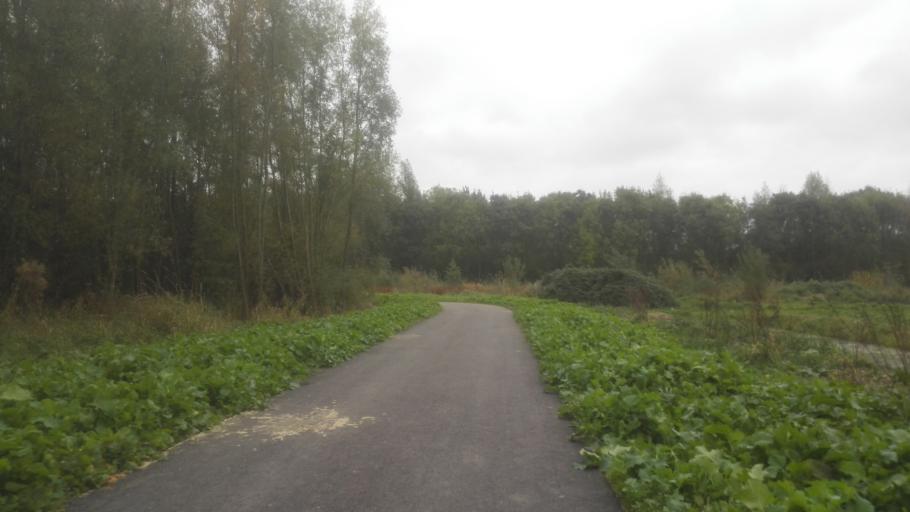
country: NL
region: South Holland
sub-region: Gemeente Delft
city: Delft
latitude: 51.9824
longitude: 4.3886
